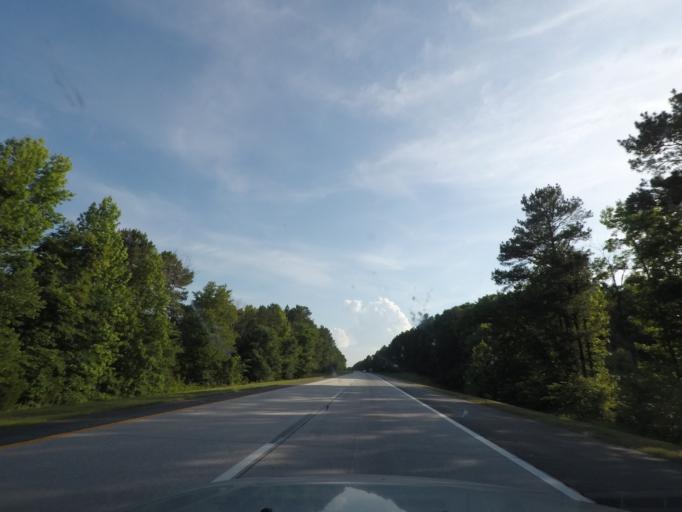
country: US
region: North Carolina
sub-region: Granville County
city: Creedmoor
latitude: 36.1827
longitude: -78.6955
